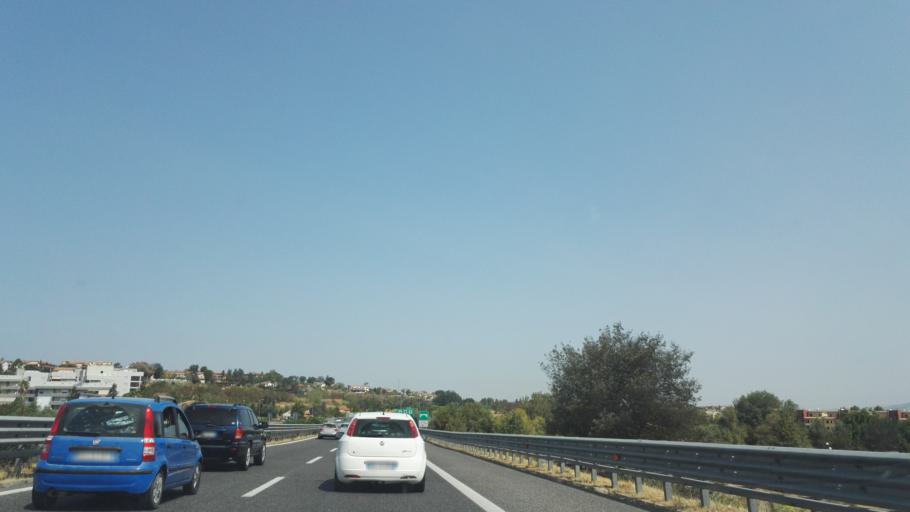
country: IT
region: Calabria
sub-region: Provincia di Cosenza
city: Quattromiglia
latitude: 39.3362
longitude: 16.2363
